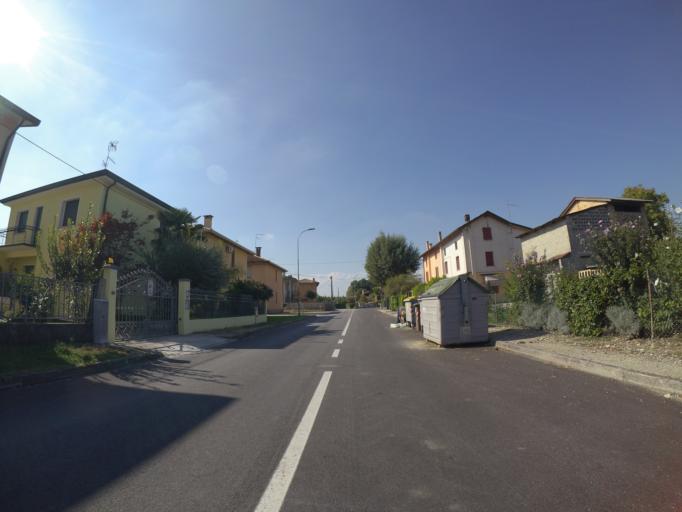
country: IT
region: Friuli Venezia Giulia
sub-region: Provincia di Udine
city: Muzzana del Turgnano
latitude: 45.8170
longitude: 13.1194
